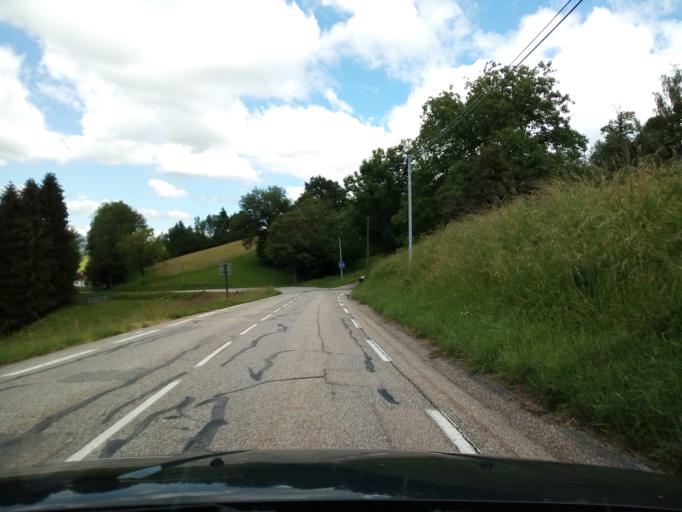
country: FR
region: Rhone-Alpes
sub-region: Departement de la Savoie
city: La Bridoire
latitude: 45.5153
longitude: 5.7689
